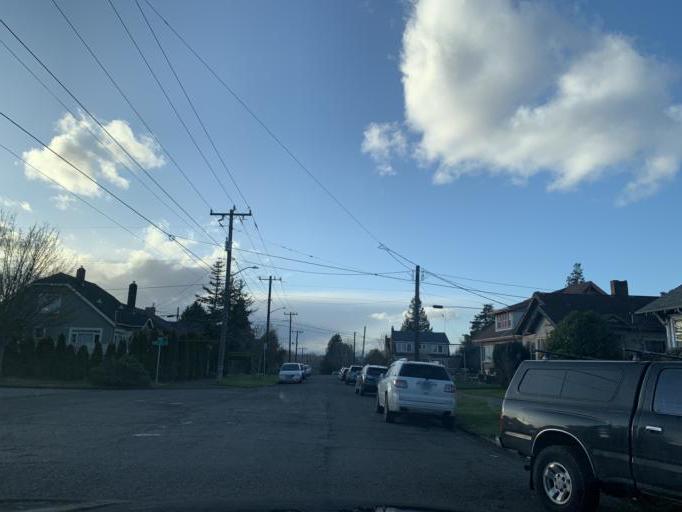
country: US
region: Washington
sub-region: King County
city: Seattle
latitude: 47.5751
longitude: -122.3109
